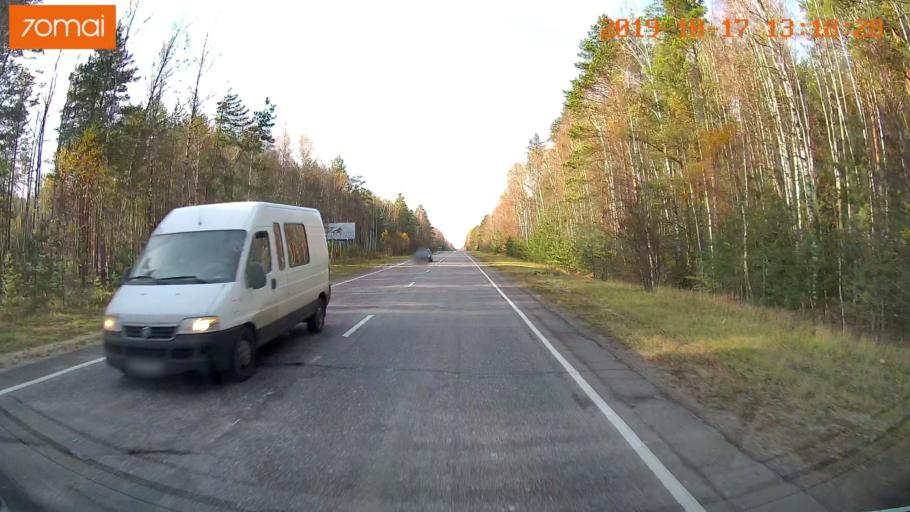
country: RU
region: Rjazan
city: Gus'-Zheleznyy
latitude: 55.0632
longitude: 41.0971
